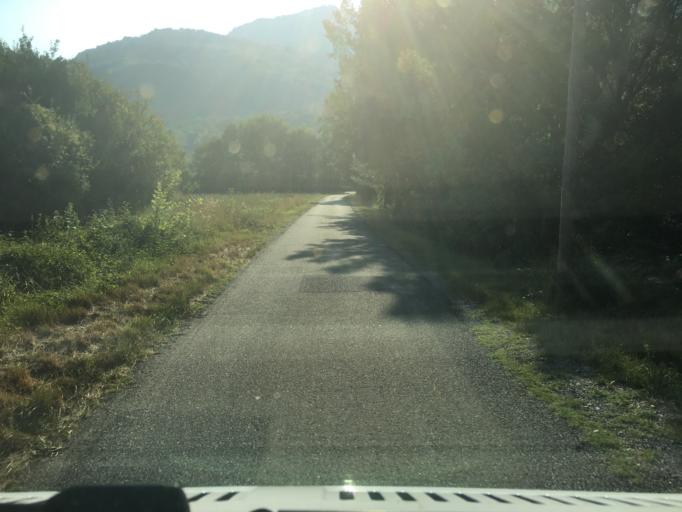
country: FR
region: Provence-Alpes-Cote d'Azur
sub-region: Departement des Alpes-de-Haute-Provence
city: Mallemoisson
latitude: 43.9395
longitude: 6.1946
